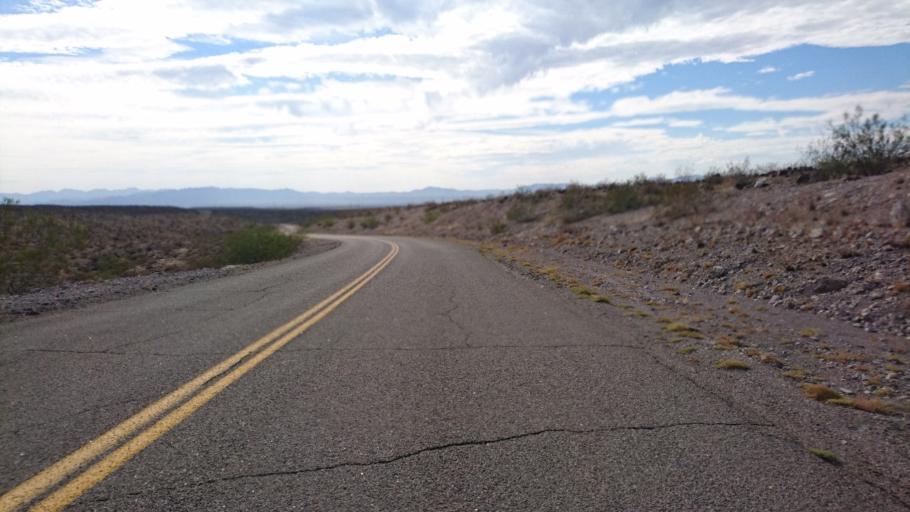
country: US
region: Arizona
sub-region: Mohave County
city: Mohave Valley
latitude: 34.8994
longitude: -114.4286
